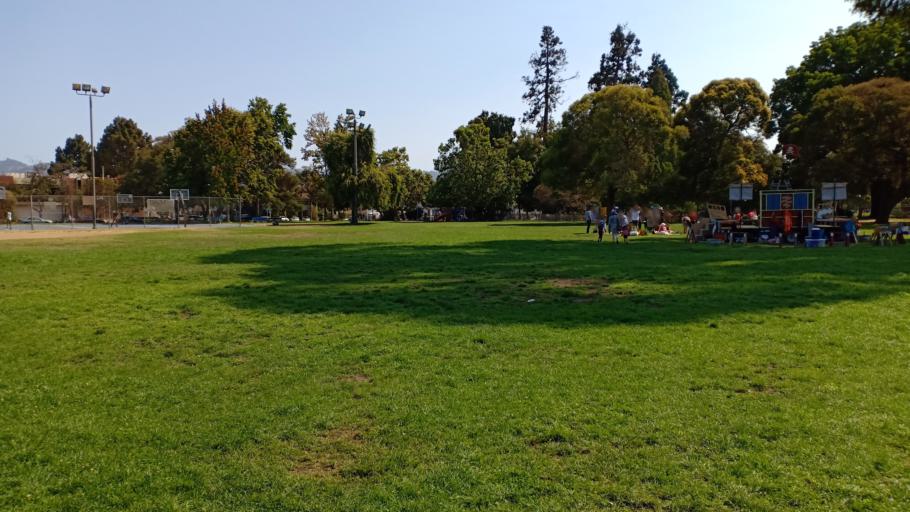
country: US
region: California
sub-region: Alameda County
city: Oakland
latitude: 37.8239
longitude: -122.2616
